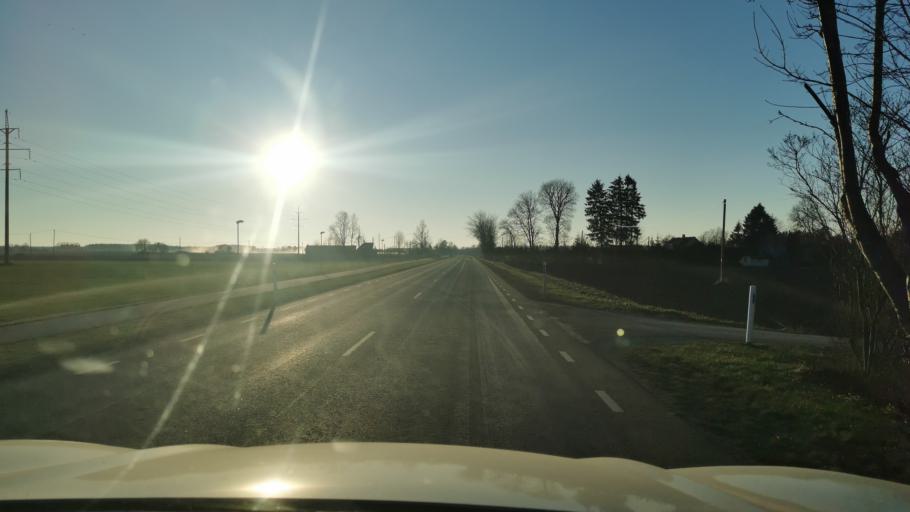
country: EE
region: Ida-Virumaa
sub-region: Kivioli linn
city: Kivioli
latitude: 59.3318
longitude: 27.0107
